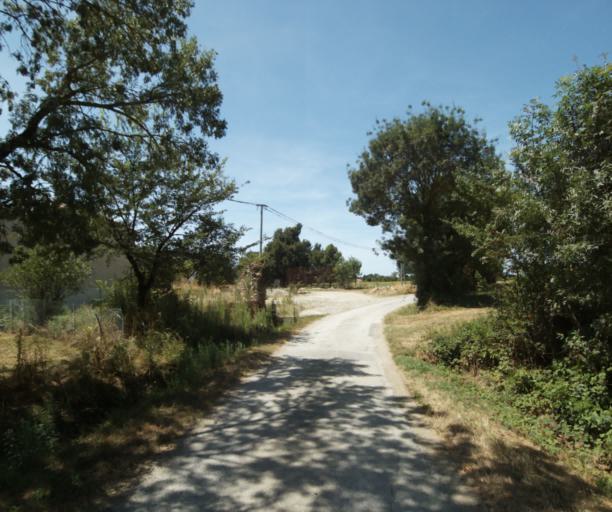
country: FR
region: Midi-Pyrenees
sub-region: Departement de la Haute-Garonne
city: Revel
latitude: 43.4991
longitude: 2.0296
